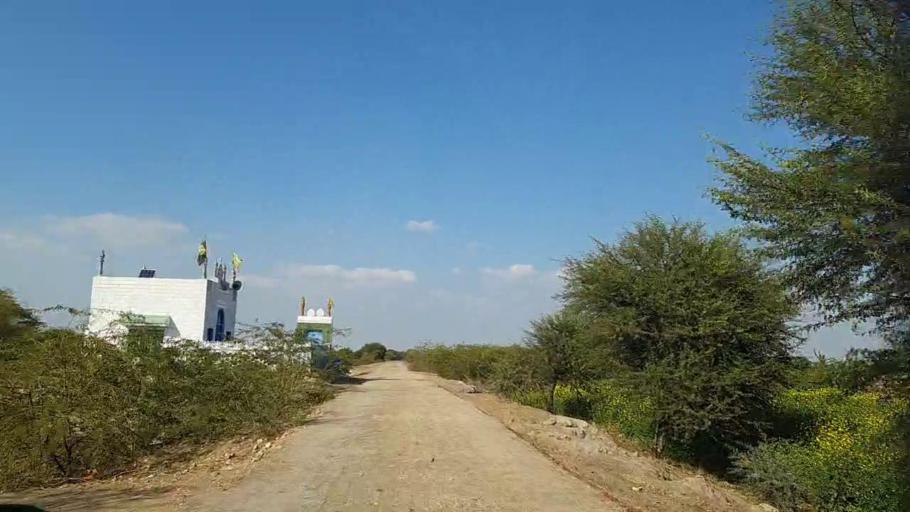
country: PK
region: Sindh
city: Pithoro
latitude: 25.6327
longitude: 69.3515
